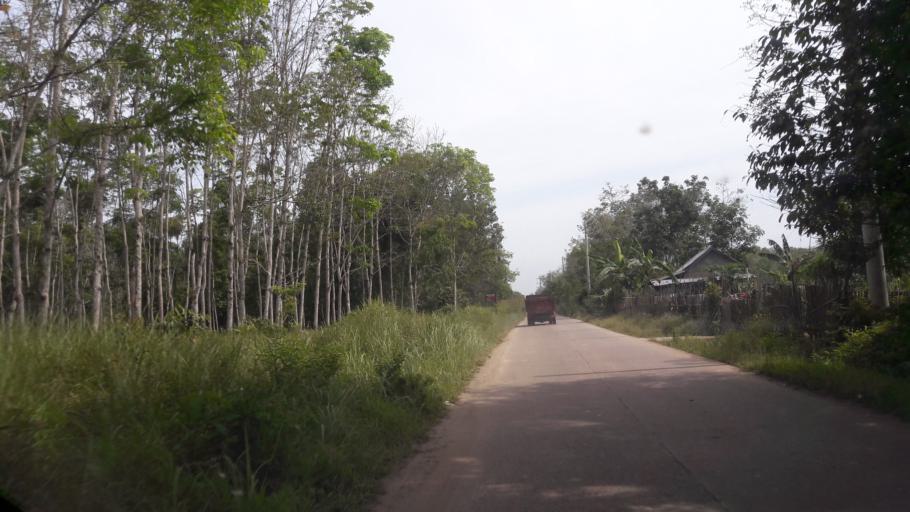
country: ID
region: South Sumatra
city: Gunungmenang
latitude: -3.2491
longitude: 104.1397
